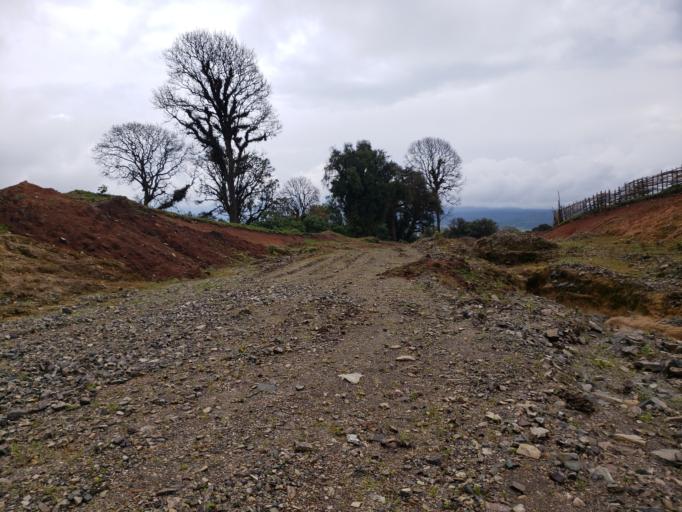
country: ET
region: Oromiya
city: Dodola
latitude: 6.6498
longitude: 39.3664
